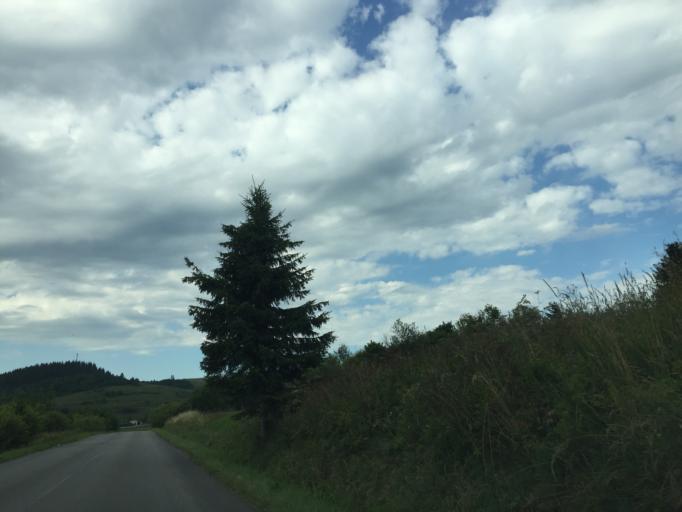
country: SK
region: Zilinsky
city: Namestovo
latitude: 49.4201
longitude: 19.3317
